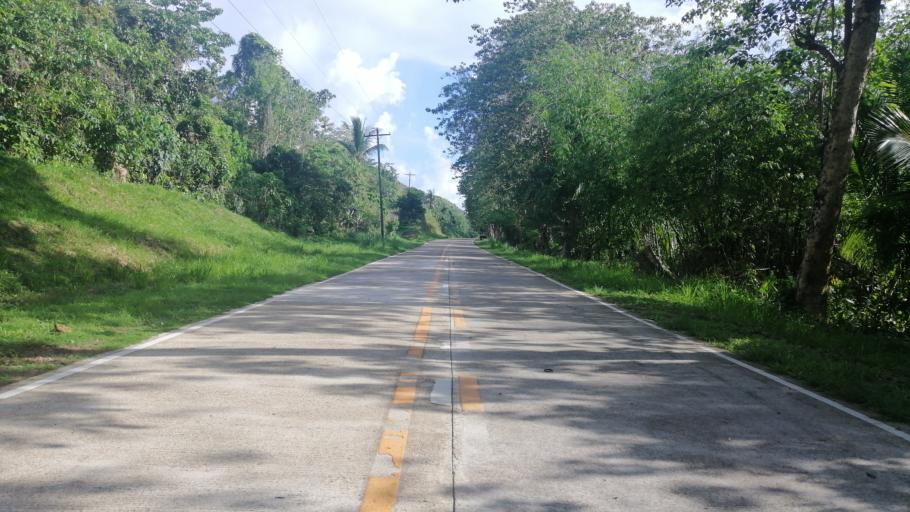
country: PH
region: Mimaropa
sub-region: Province of Palawan
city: Salvacion
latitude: 12.1194
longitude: 119.9390
